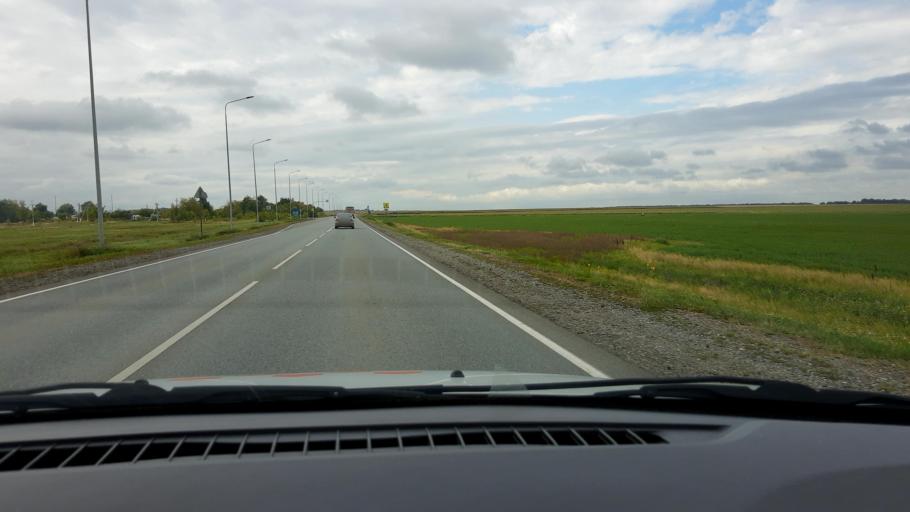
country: RU
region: Tatarstan
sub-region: Alekseyevskiy Rayon
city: Alekseyevskoye
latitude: 55.3130
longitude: 50.2904
